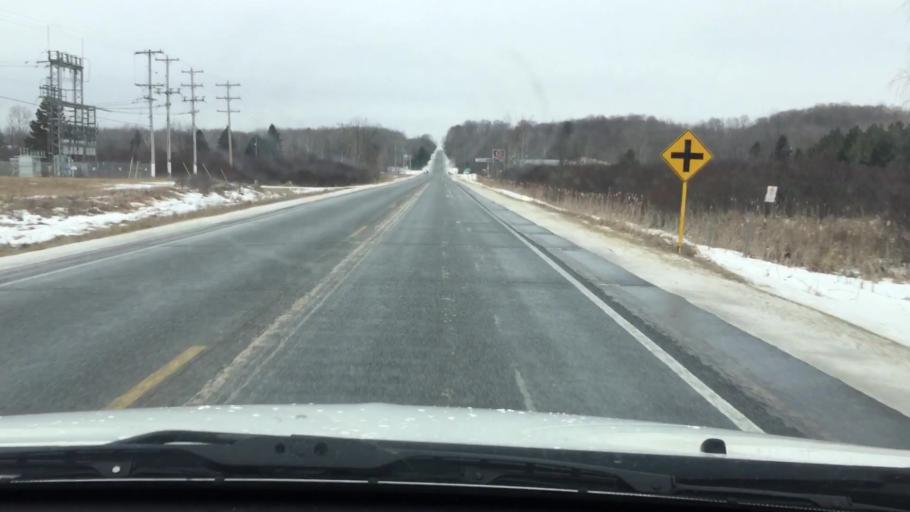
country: US
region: Michigan
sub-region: Wexford County
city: Cadillac
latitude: 44.1054
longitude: -85.4443
